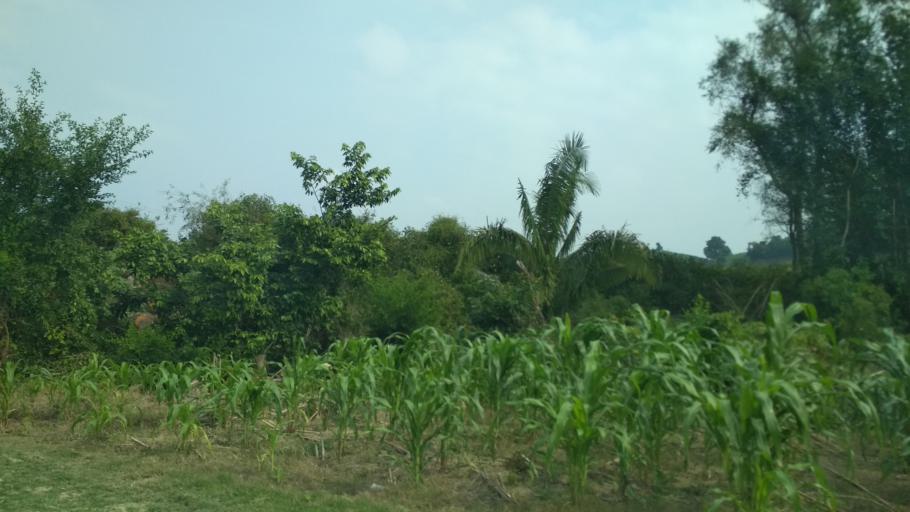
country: MM
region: Kayah
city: Loikaw
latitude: 20.2047
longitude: 97.3183
